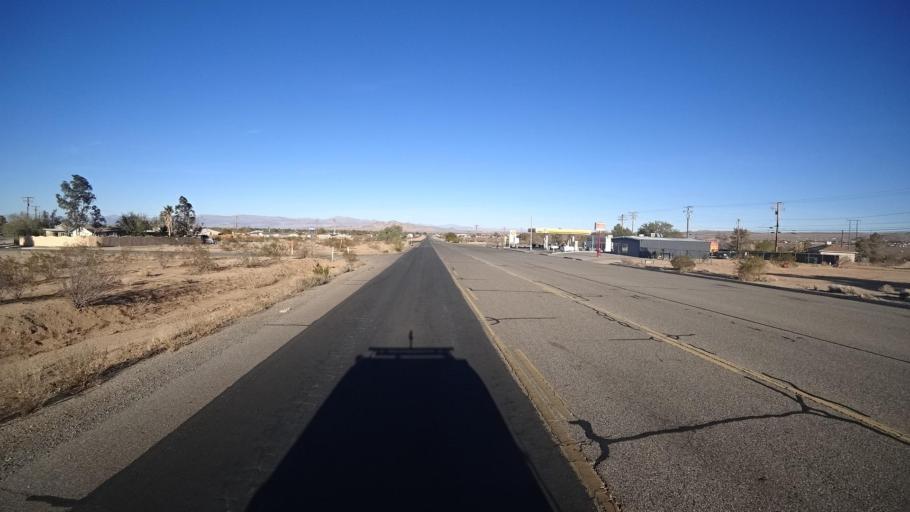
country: US
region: California
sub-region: Kern County
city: Ridgecrest
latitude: 35.5941
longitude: -117.6902
